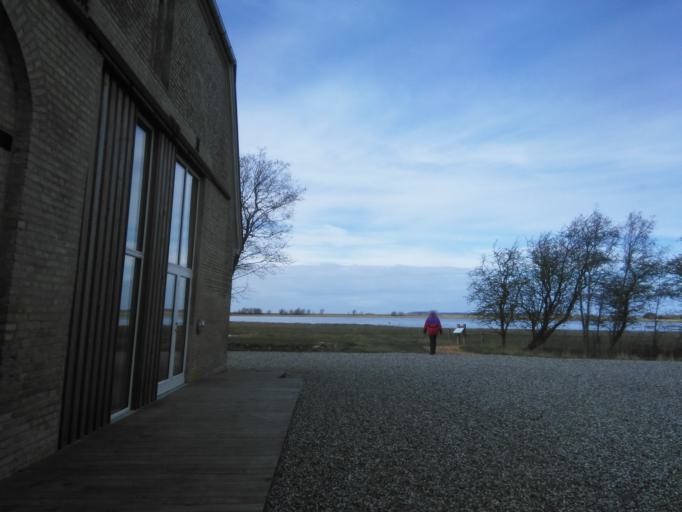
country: DK
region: South Denmark
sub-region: Nordfyns Kommune
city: Bogense
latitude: 55.5802
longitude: 10.1589
